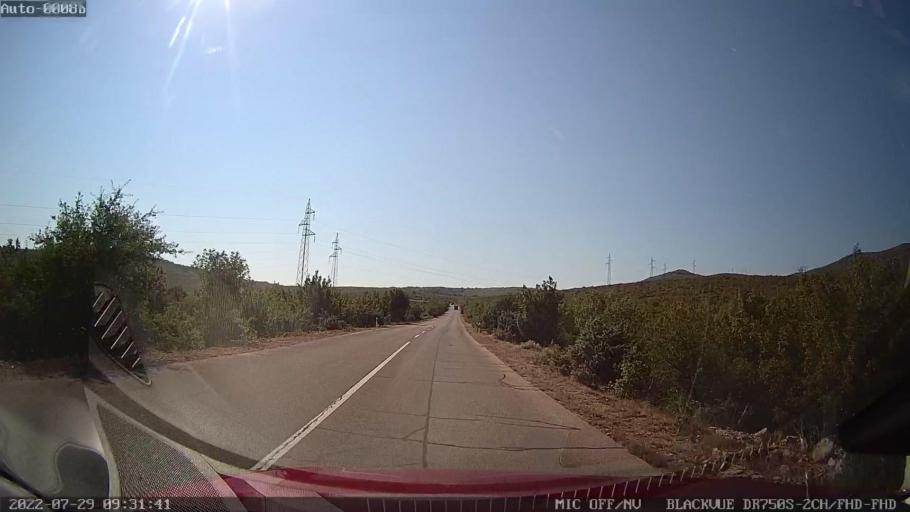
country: HR
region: Zadarska
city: Obrovac
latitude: 44.1878
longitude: 15.7021
